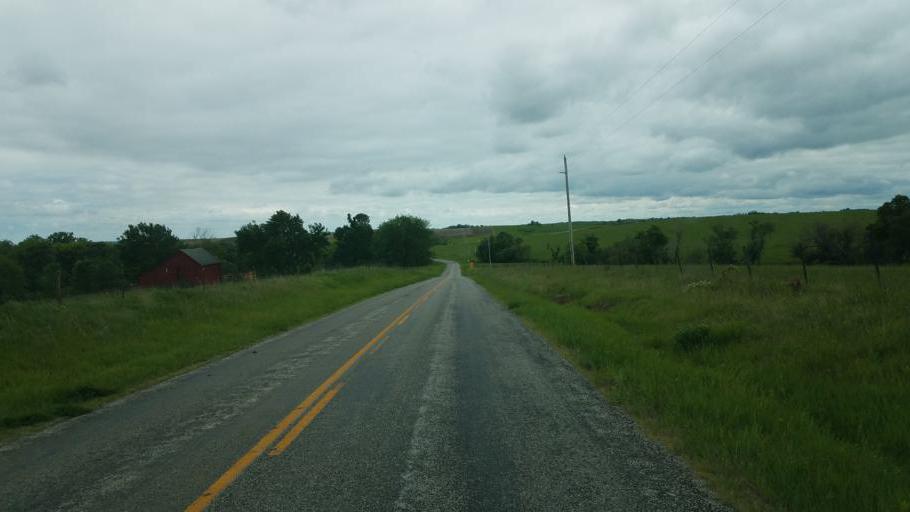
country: US
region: Iowa
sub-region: Decatur County
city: Lamoni
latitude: 40.5364
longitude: -93.8415
